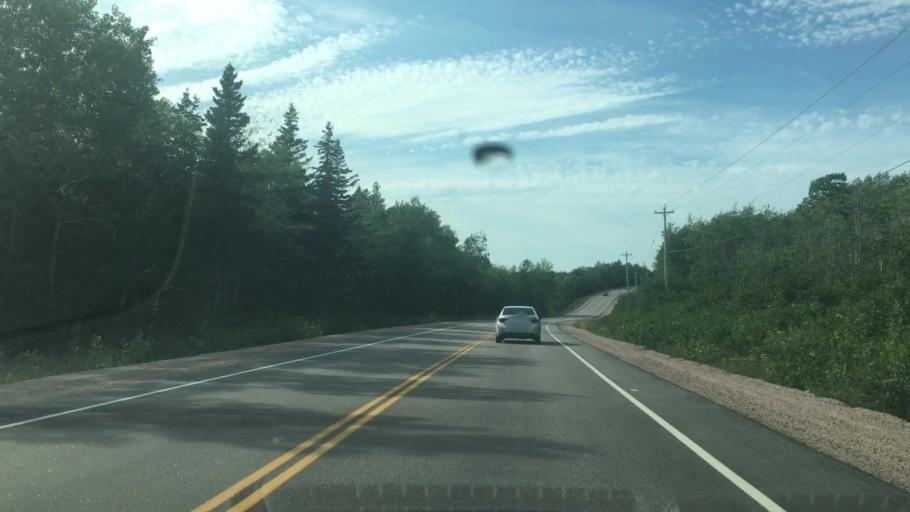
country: CA
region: Nova Scotia
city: Sydney Mines
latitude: 46.8203
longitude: -60.3534
